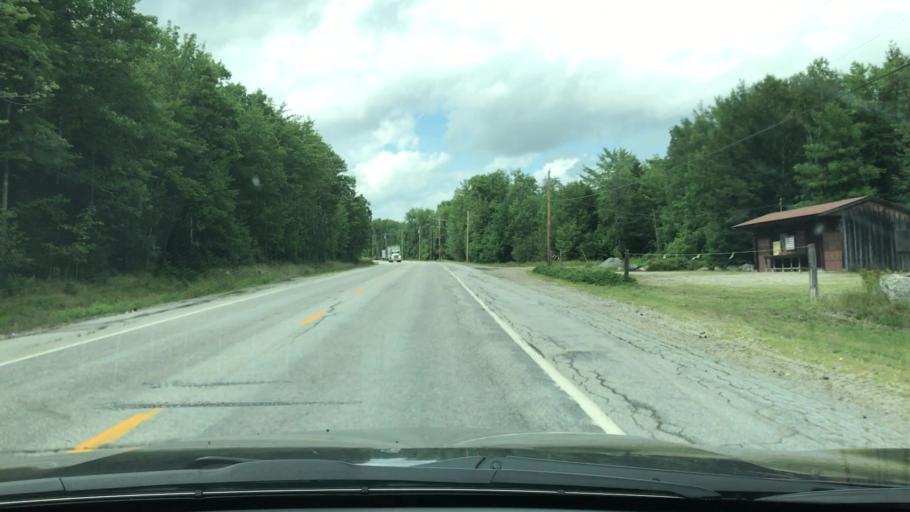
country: US
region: Maine
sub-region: Oxford County
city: West Paris
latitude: 44.3807
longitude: -70.6181
